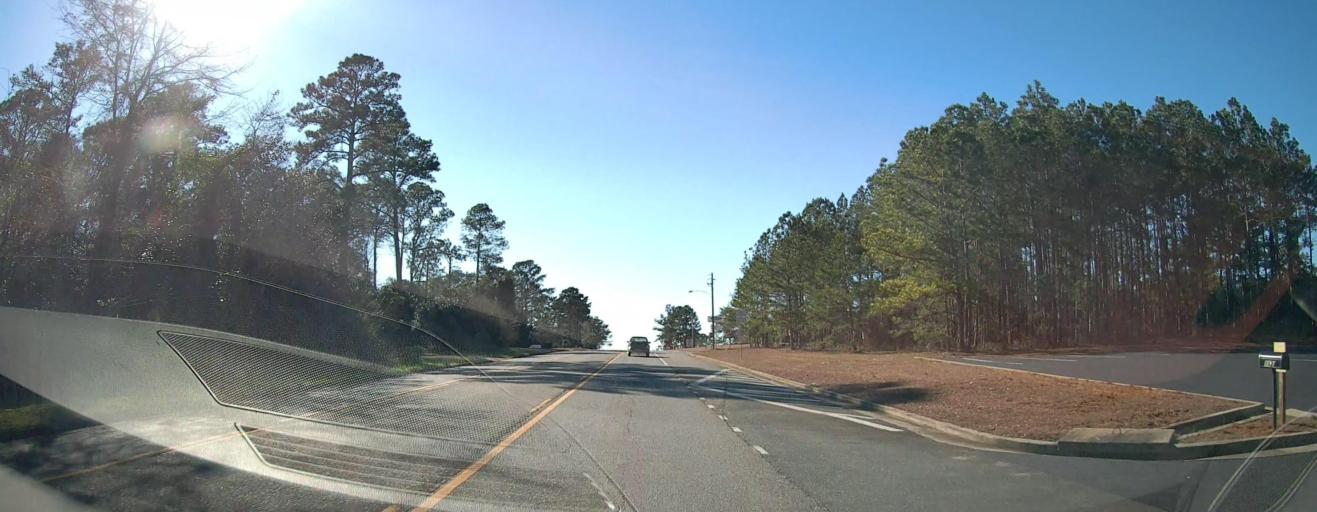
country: US
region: Georgia
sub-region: Sumter County
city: Americus
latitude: 32.0711
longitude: -84.2007
